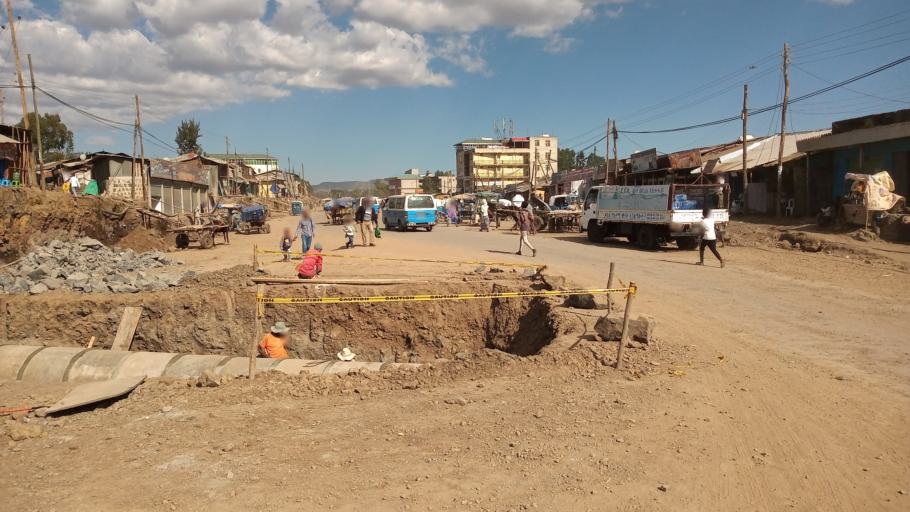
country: ET
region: Amhara
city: Gondar
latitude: 12.5531
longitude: 37.4267
